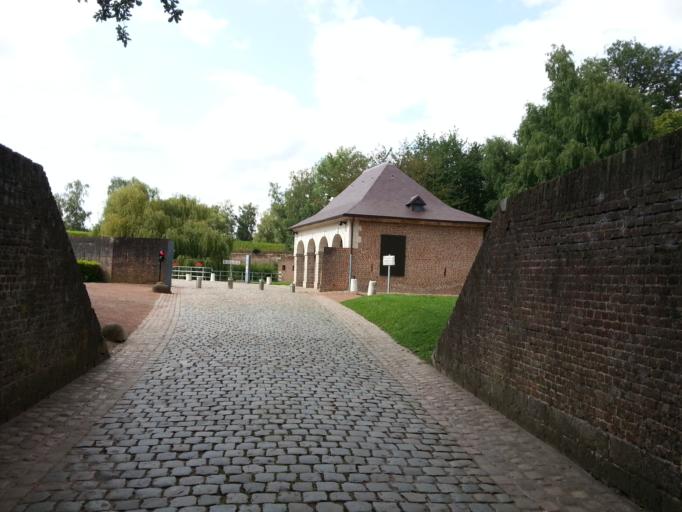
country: FR
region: Nord-Pas-de-Calais
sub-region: Departement du Nord
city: Lille
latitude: 50.6400
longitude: 3.0479
